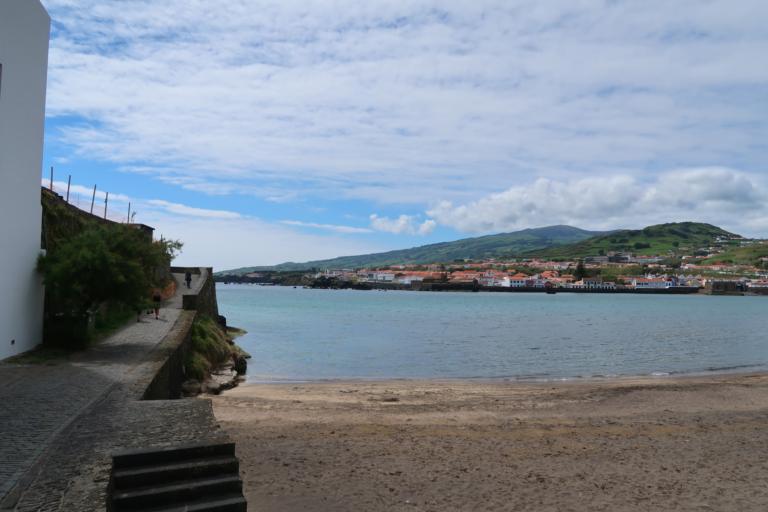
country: PT
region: Azores
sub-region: Horta
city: Horta
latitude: 38.5233
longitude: -28.6254
